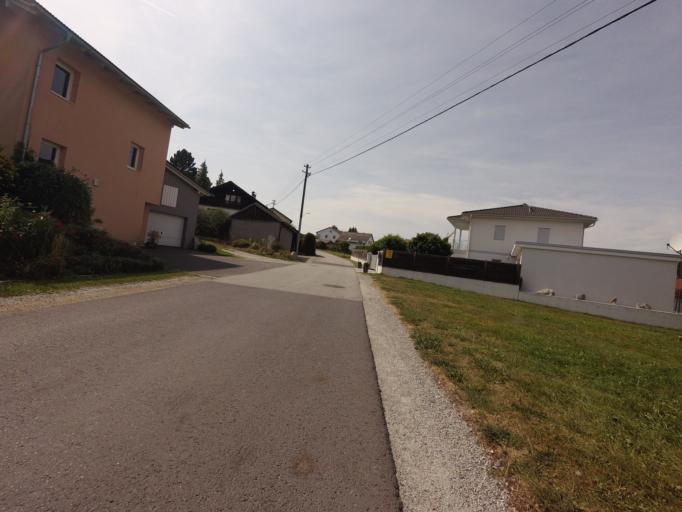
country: AT
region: Upper Austria
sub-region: Politischer Bezirk Urfahr-Umgebung
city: Bad Leonfelden
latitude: 48.5224
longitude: 14.3003
